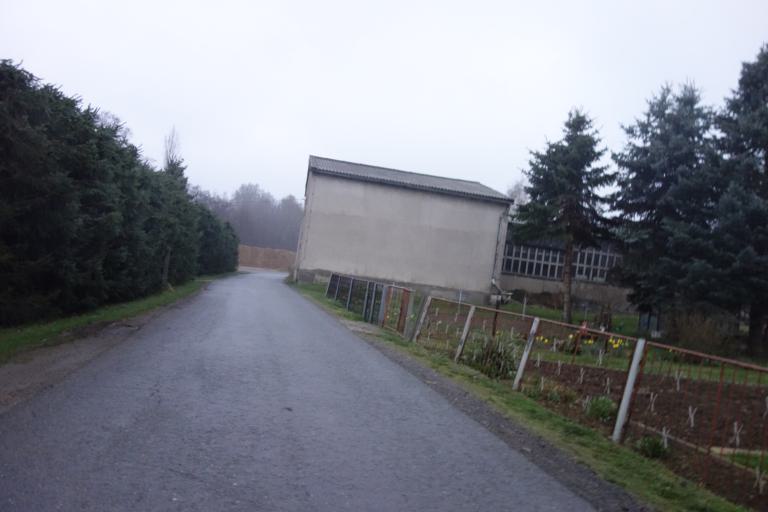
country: DE
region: Saxony
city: Freiberg
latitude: 50.8960
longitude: 13.3598
